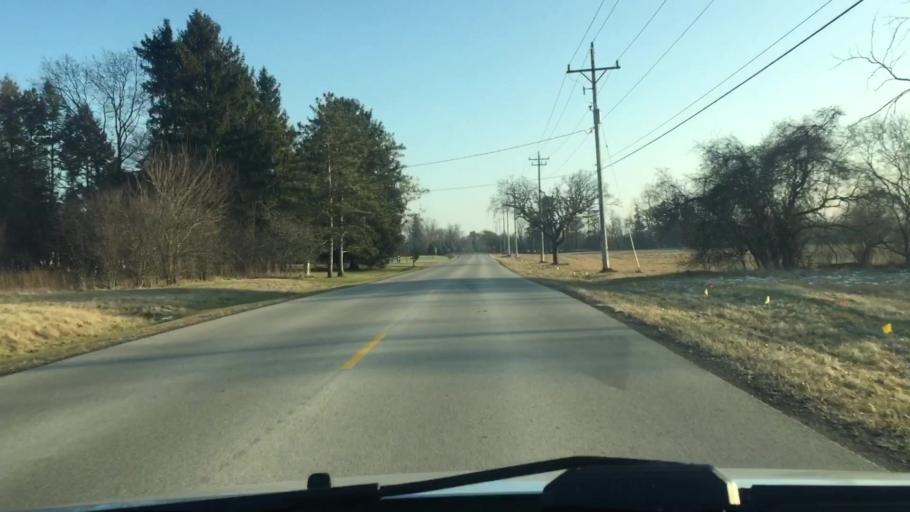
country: US
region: Wisconsin
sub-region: Waukesha County
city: Dousman
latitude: 43.0372
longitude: -88.4831
